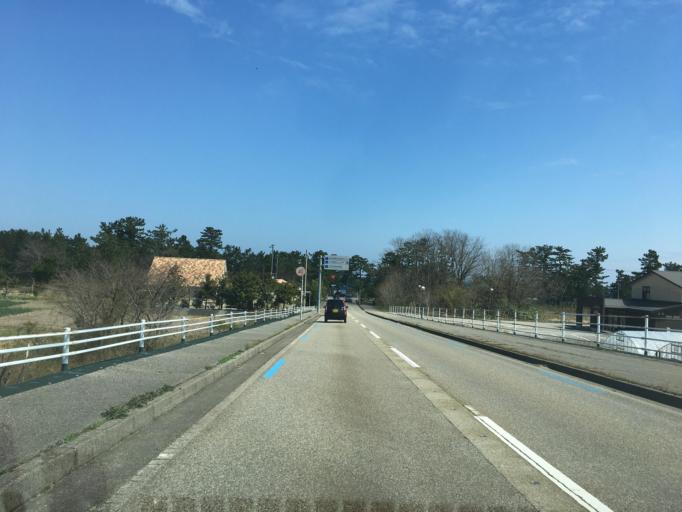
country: JP
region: Toyama
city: Himi
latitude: 36.8334
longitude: 137.0073
